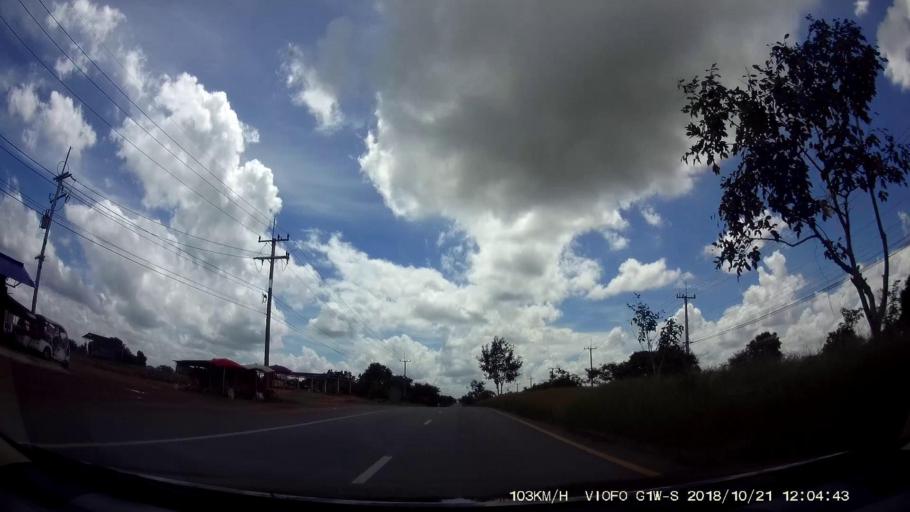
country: TH
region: Chaiyaphum
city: Chatturat
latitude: 15.4904
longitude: 101.8218
